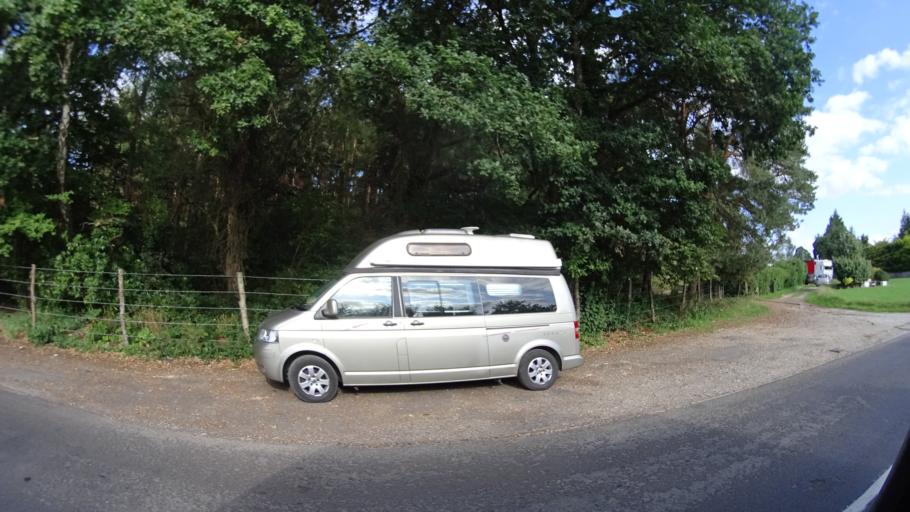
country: GB
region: England
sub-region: Dorset
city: Lytchett Matravers
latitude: 50.7510
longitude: -2.0437
